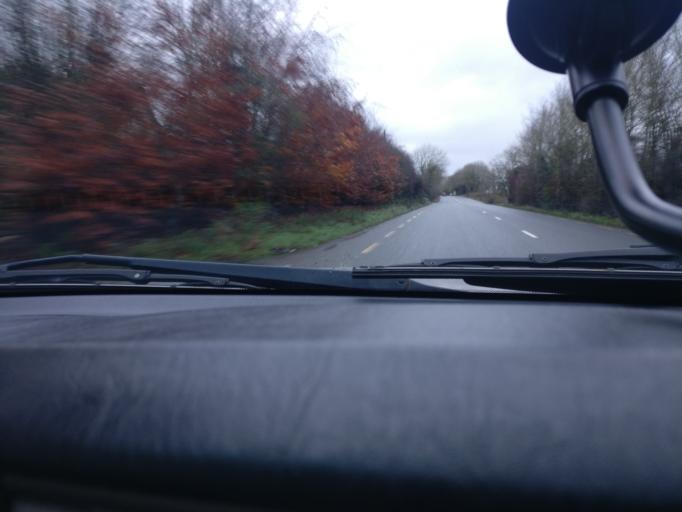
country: IE
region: Leinster
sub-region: Kildare
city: Kilcock
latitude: 53.4161
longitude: -6.7236
